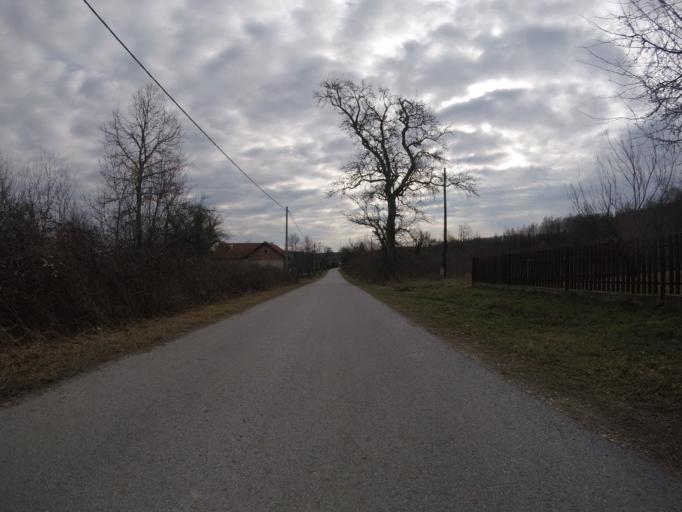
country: HR
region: Sisacko-Moslavacka
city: Glina
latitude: 45.4335
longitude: 16.0805
